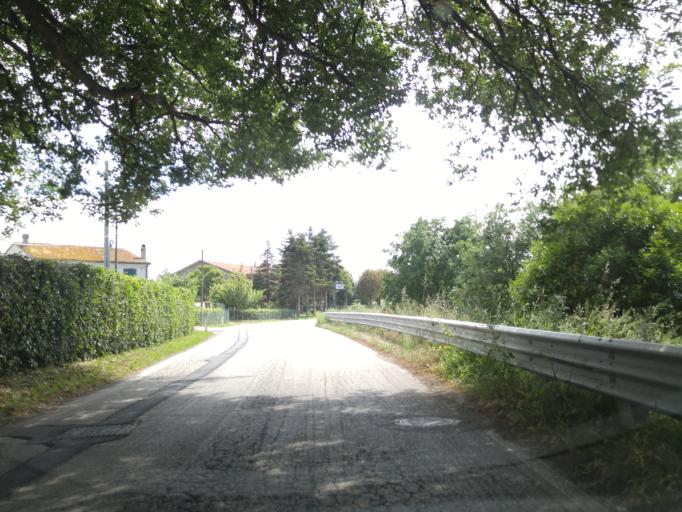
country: IT
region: The Marches
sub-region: Provincia di Pesaro e Urbino
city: Bellocchi
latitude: 43.8024
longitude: 13.0432
